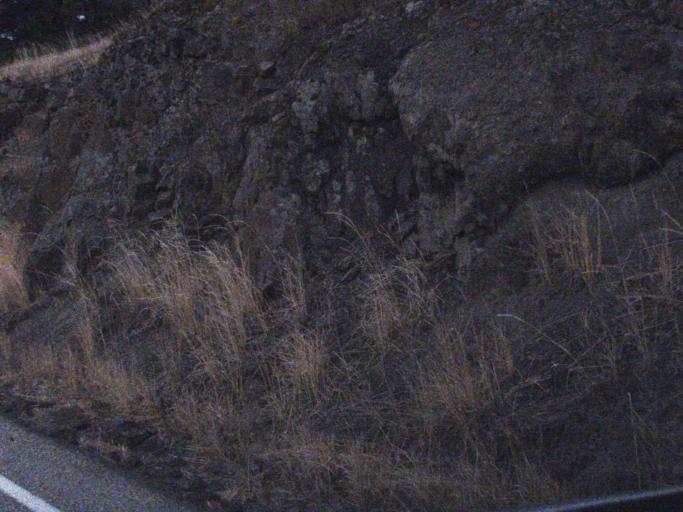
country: US
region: Washington
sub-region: Ferry County
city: Republic
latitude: 48.6443
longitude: -118.6850
